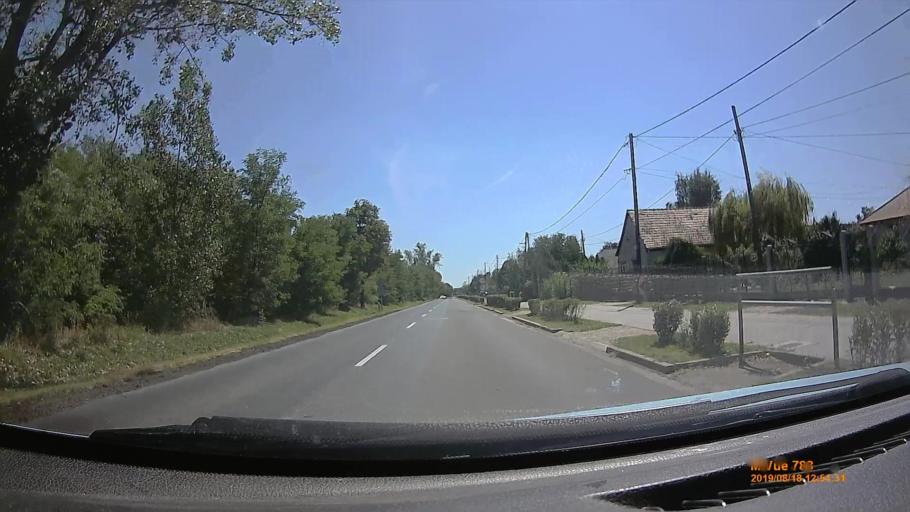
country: HU
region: Fejer
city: Aba
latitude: 47.0409
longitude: 18.5320
